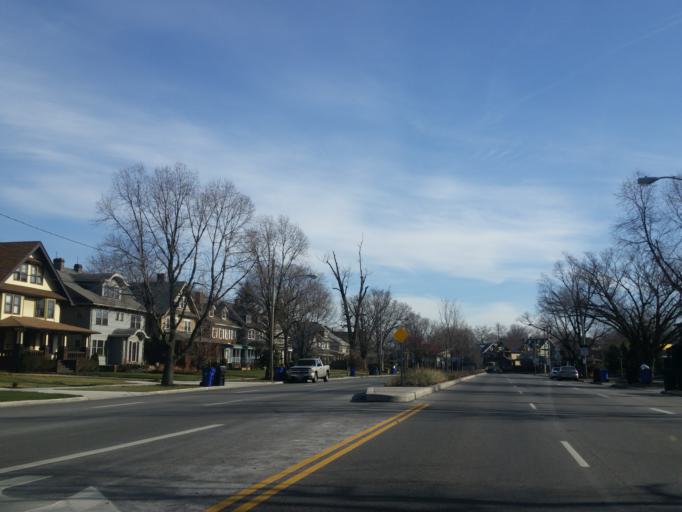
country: US
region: Ohio
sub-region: Cuyahoga County
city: Lakewood
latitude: 41.4843
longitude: -81.7514
